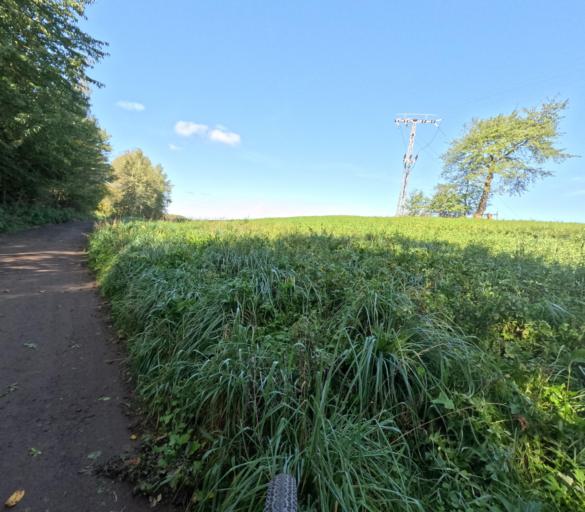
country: DE
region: Saxony
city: Moritzburg
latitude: 51.1722
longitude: 13.7142
